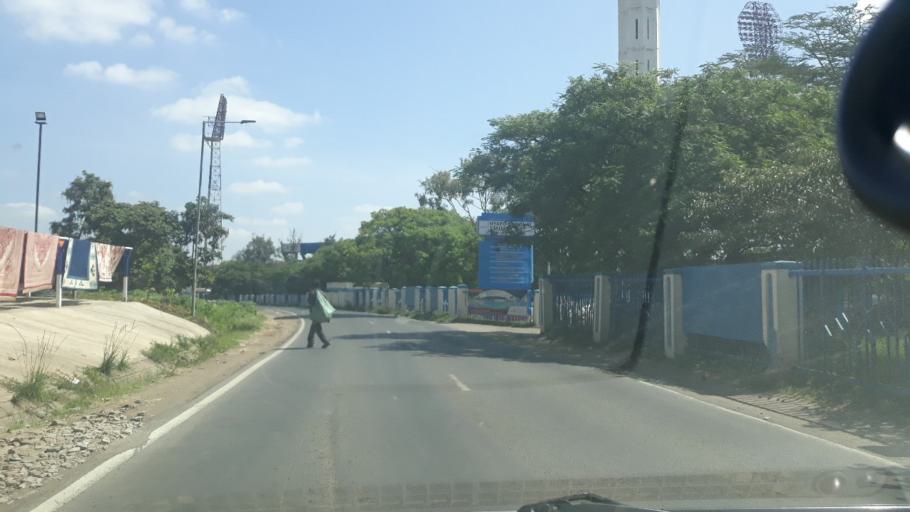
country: KE
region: Nairobi Area
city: Nairobi
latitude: -1.3050
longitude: 36.8226
